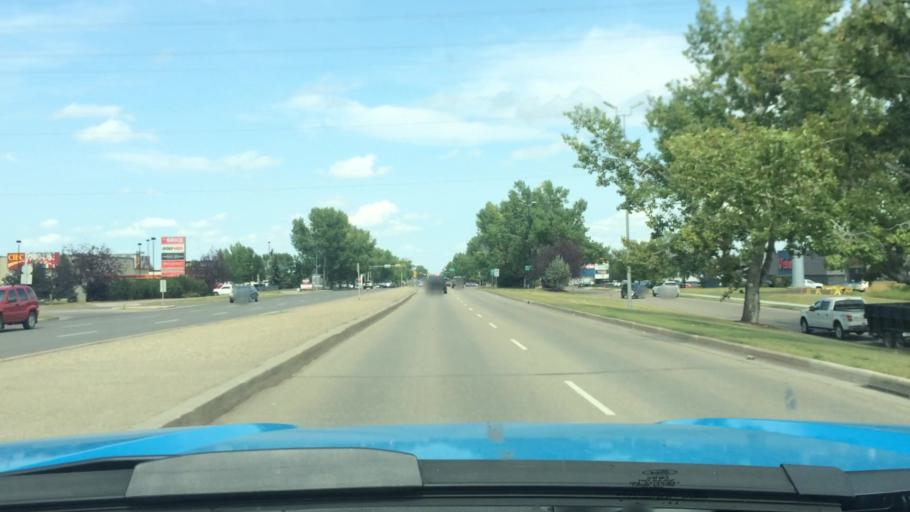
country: CA
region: Alberta
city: Red Deer
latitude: 52.2365
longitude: -113.8139
